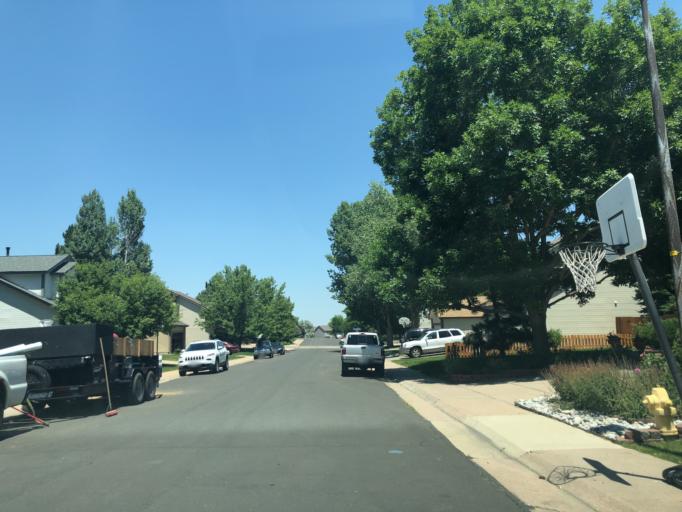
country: US
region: Colorado
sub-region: Arapahoe County
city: Dove Valley
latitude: 39.6172
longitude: -104.7575
